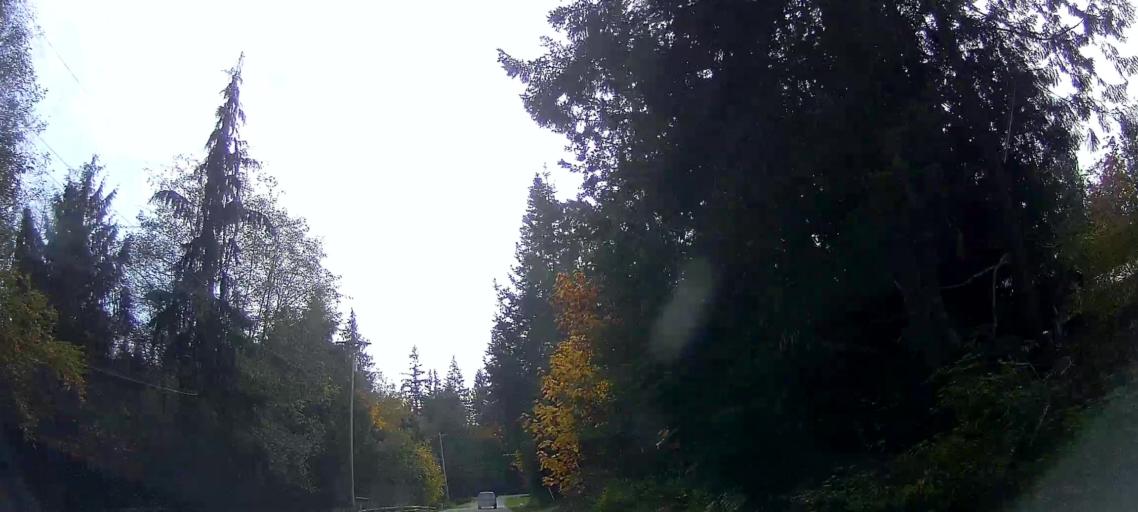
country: US
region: Washington
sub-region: Snohomish County
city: Stanwood
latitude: 48.2853
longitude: -122.3442
